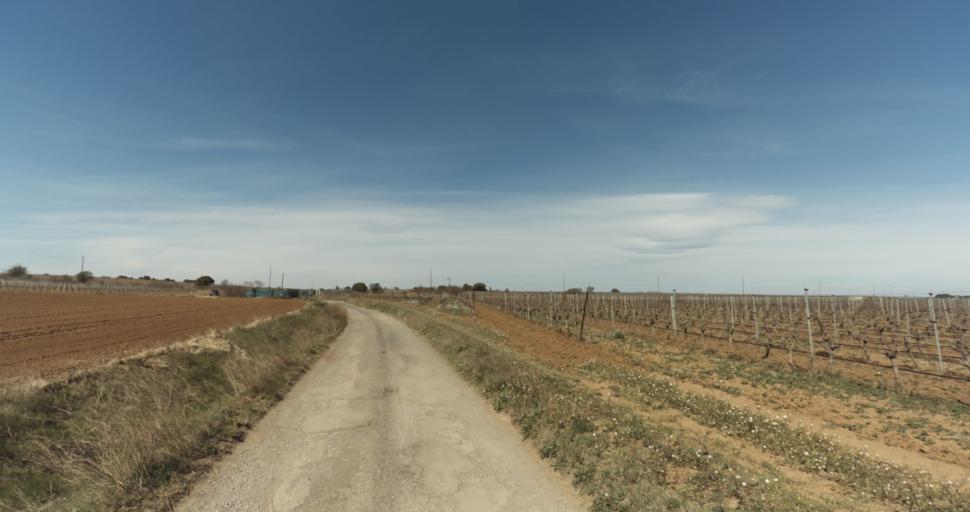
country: FR
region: Languedoc-Roussillon
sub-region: Departement de l'Herault
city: Marseillan
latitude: 43.3720
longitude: 3.5408
